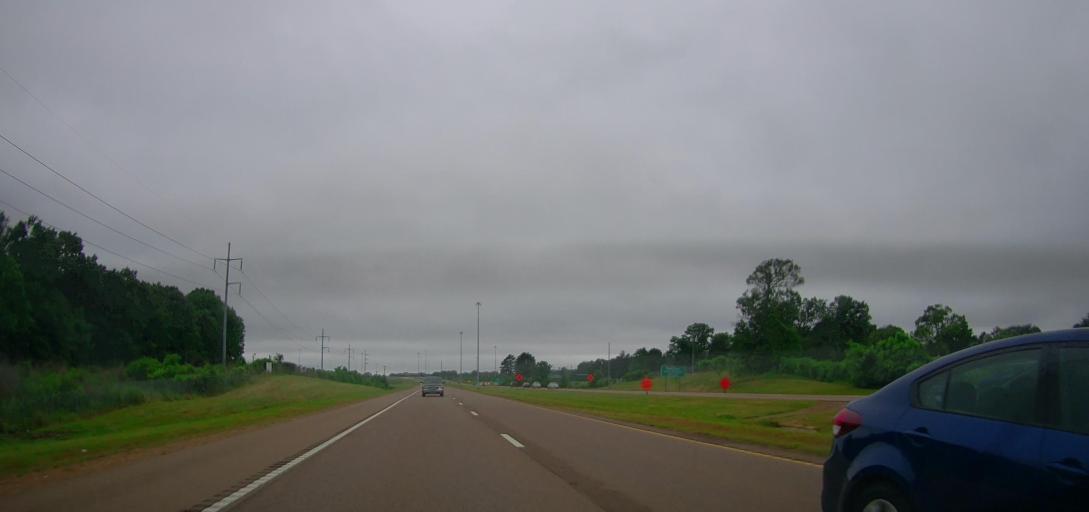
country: US
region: Mississippi
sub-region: De Soto County
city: Olive Branch
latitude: 34.9690
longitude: -89.8198
